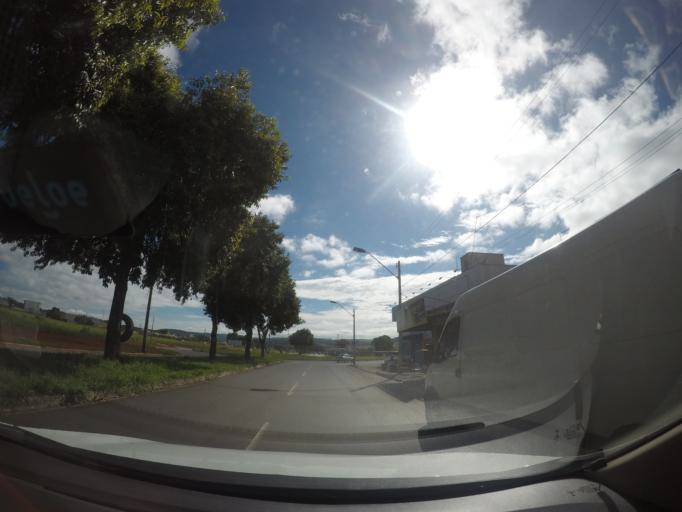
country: BR
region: Goias
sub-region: Goiania
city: Goiania
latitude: -16.6545
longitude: -49.1767
